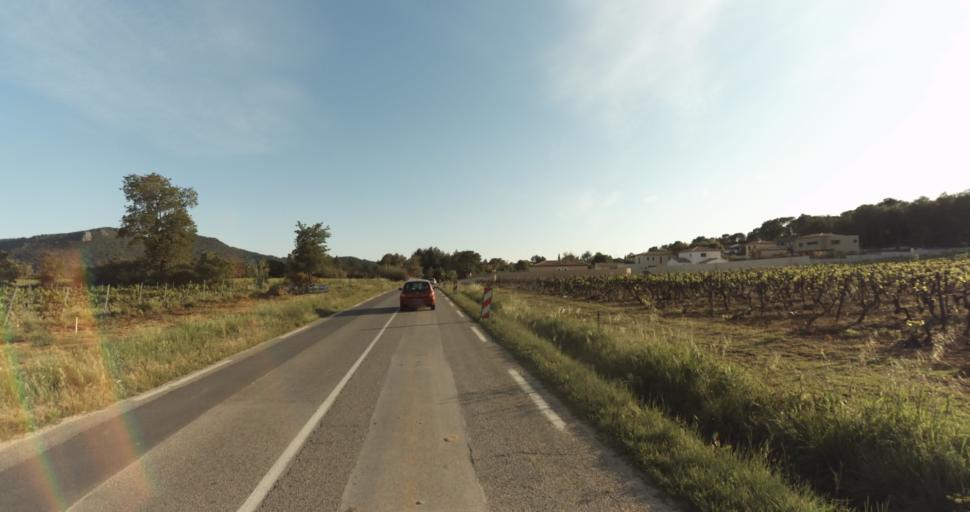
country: FR
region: Provence-Alpes-Cote d'Azur
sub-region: Departement du Var
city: La Crau
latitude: 43.1594
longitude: 6.0977
